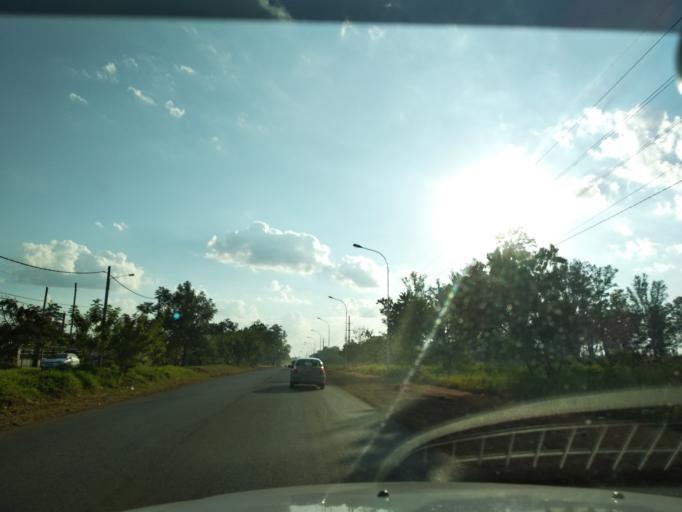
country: AR
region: Misiones
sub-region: Departamento de Capital
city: Posadas
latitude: -27.4320
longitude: -55.9408
